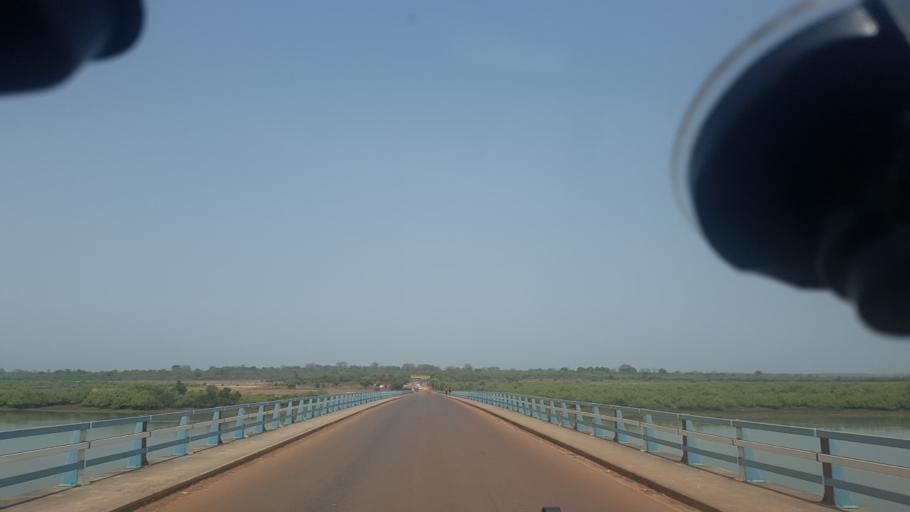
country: GW
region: Bissau
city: Bissau
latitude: 12.0159
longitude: -15.6896
